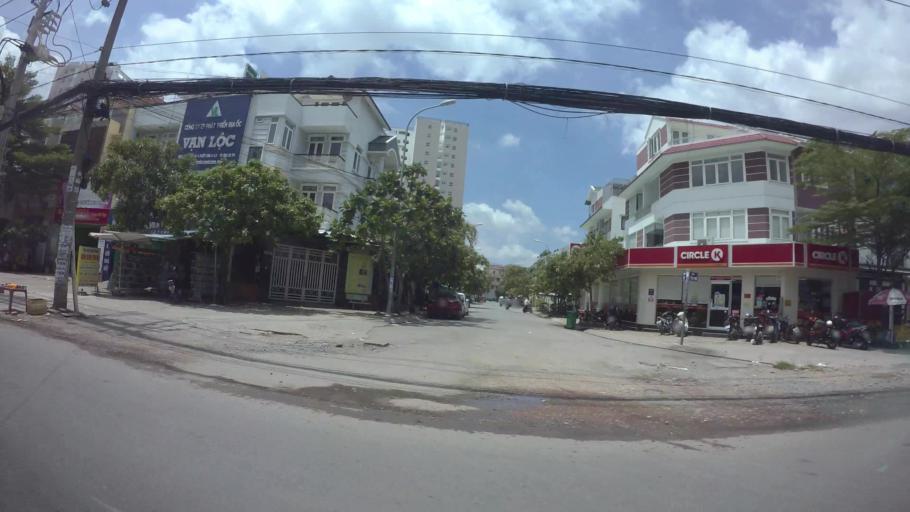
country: VN
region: Ho Chi Minh City
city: Quan Chin
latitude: 10.8287
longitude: 106.7726
